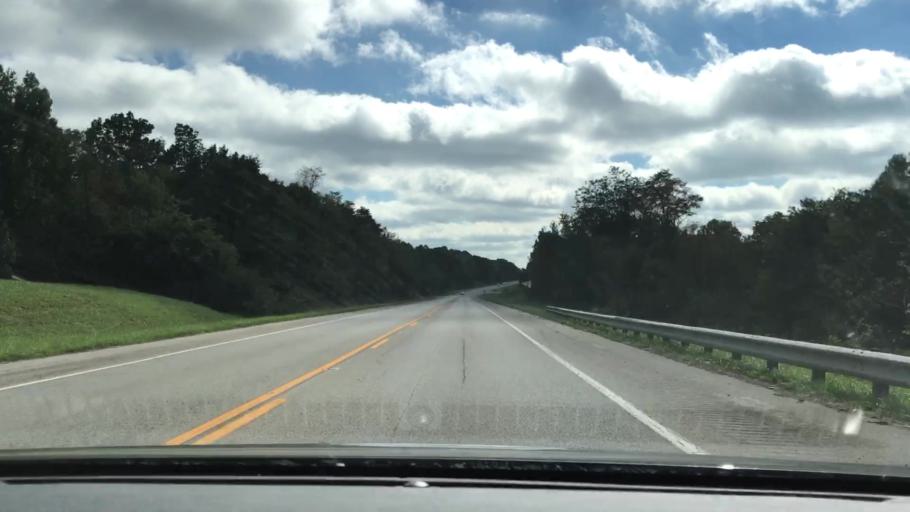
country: US
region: Kentucky
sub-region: McCreary County
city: Pine Knot
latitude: 36.6273
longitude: -84.4360
